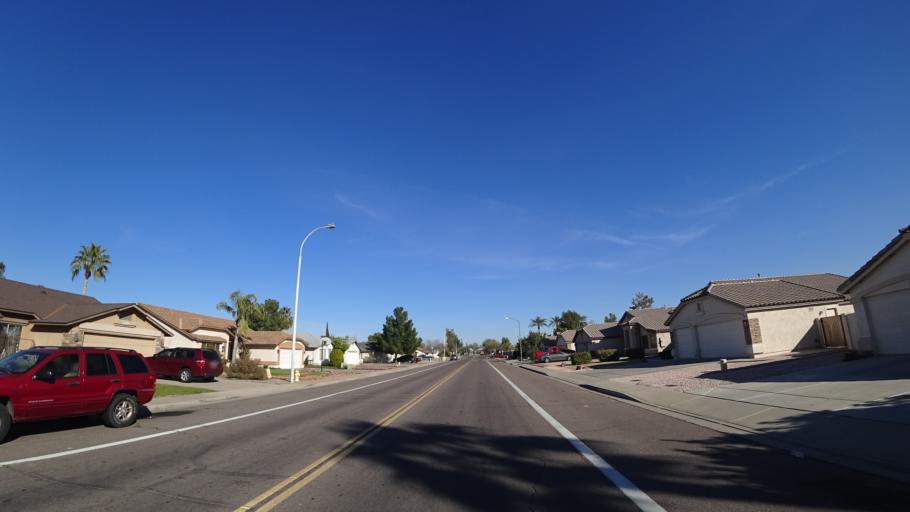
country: US
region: Arizona
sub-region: Maricopa County
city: Peoria
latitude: 33.5305
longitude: -112.2408
